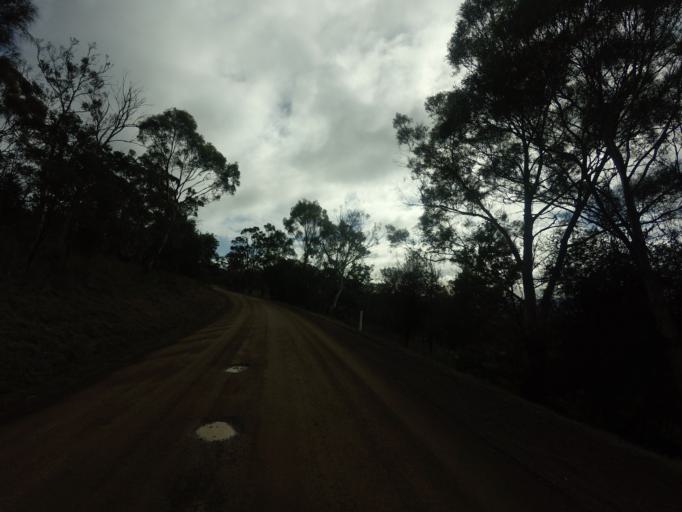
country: AU
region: Tasmania
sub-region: Derwent Valley
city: New Norfolk
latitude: -42.7380
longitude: 146.8702
